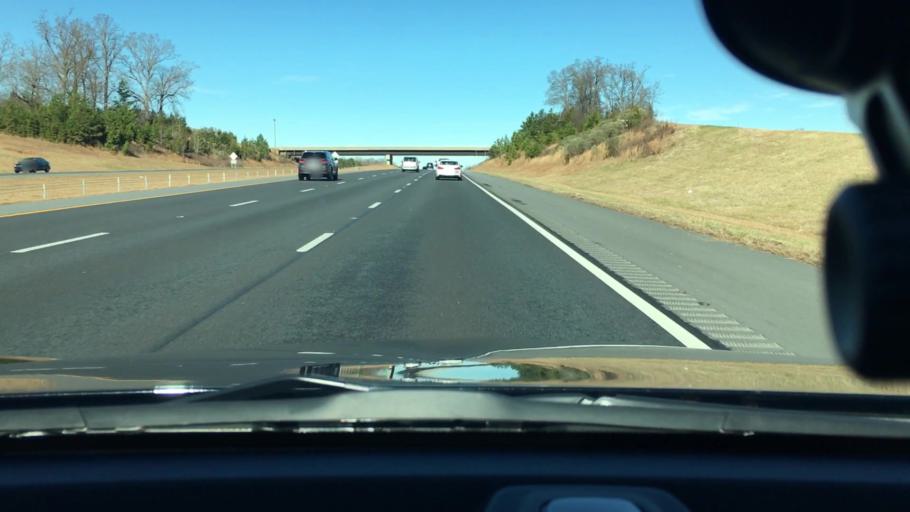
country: US
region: North Carolina
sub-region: Cabarrus County
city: Harrisburg
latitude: 35.2817
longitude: -80.6739
